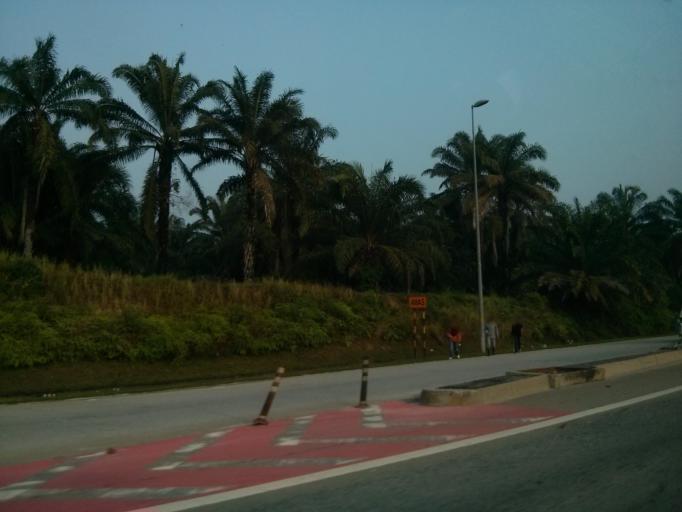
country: MY
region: Negeri Sembilan
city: Kampung Baharu Nilai
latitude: 2.8204
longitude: 101.6934
